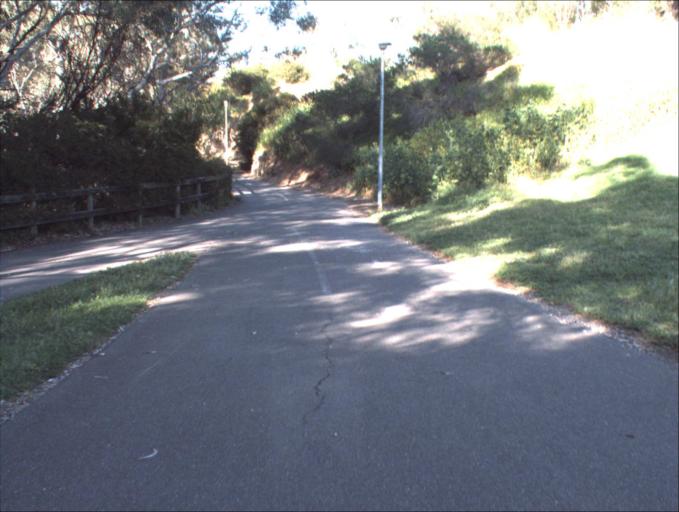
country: AU
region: South Australia
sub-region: Port Adelaide Enfield
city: Klemzig
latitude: -34.8742
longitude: 138.6481
